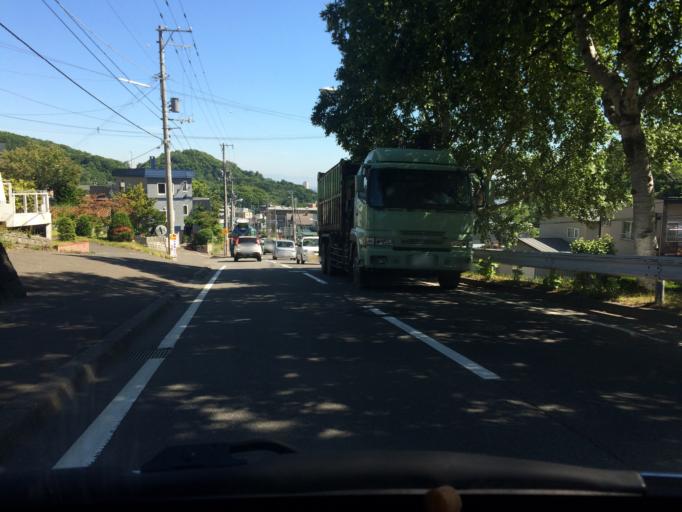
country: JP
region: Hokkaido
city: Sapporo
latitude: 43.0431
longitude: 141.2919
